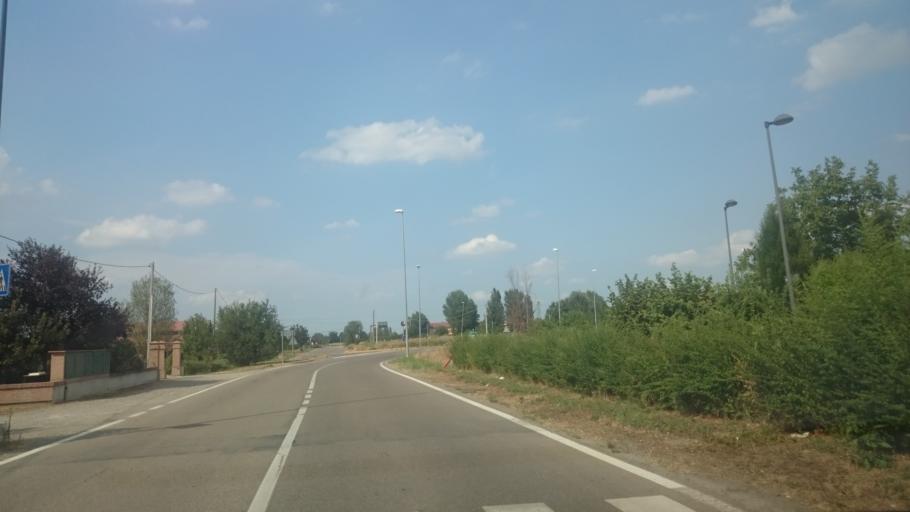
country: IT
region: Emilia-Romagna
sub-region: Provincia di Reggio Emilia
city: Salvaterra
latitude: 44.6044
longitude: 10.7755
